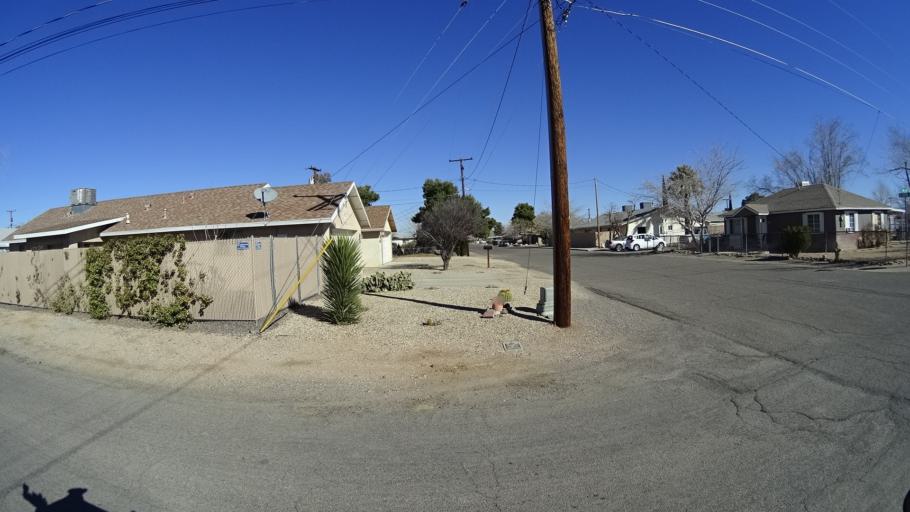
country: US
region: Arizona
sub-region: Mohave County
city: Kingman
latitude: 35.2060
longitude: -114.0271
